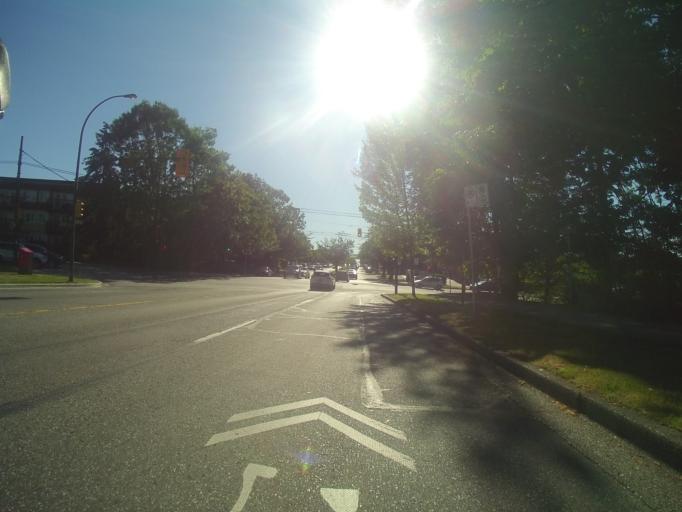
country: CA
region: British Columbia
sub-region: Fraser Valley Regional District
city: North Vancouver
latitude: 49.2507
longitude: -123.0436
